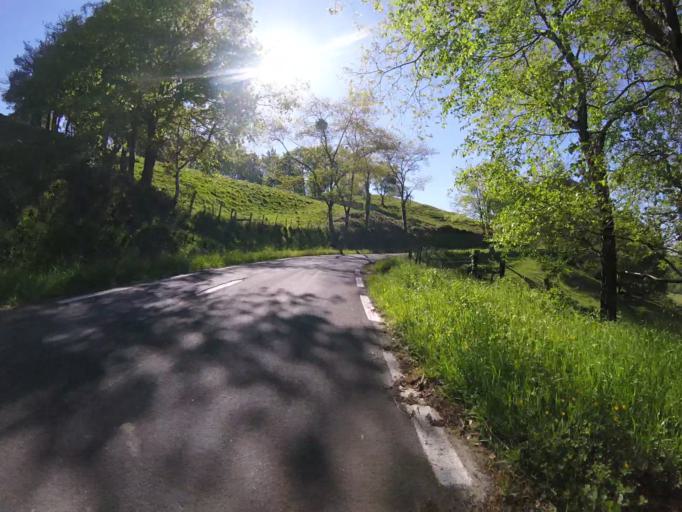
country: ES
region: Basque Country
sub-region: Provincia de Guipuzcoa
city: Aizarnazabal
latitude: 43.2161
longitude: -2.2097
